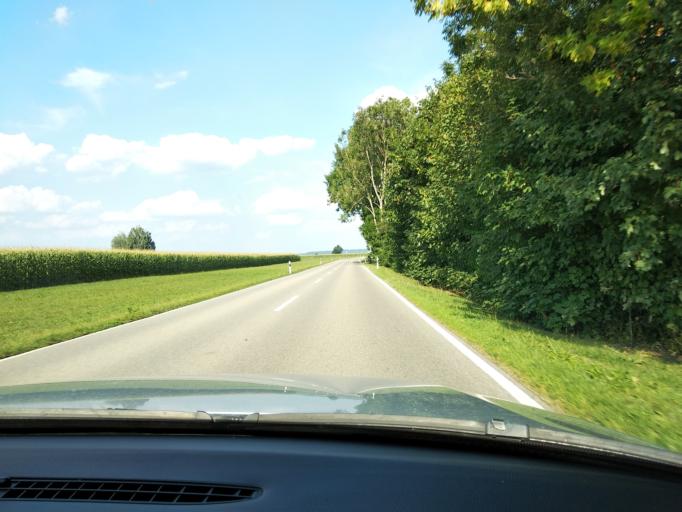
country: DE
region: Bavaria
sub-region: Swabia
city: Memmingerberg
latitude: 47.9937
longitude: 10.2227
